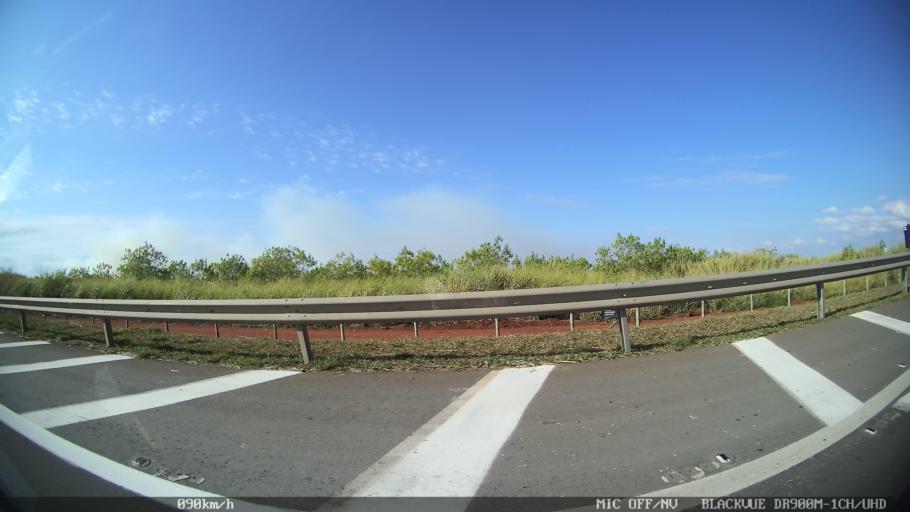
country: BR
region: Sao Paulo
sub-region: Piracicaba
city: Piracicaba
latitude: -22.7164
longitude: -47.6060
